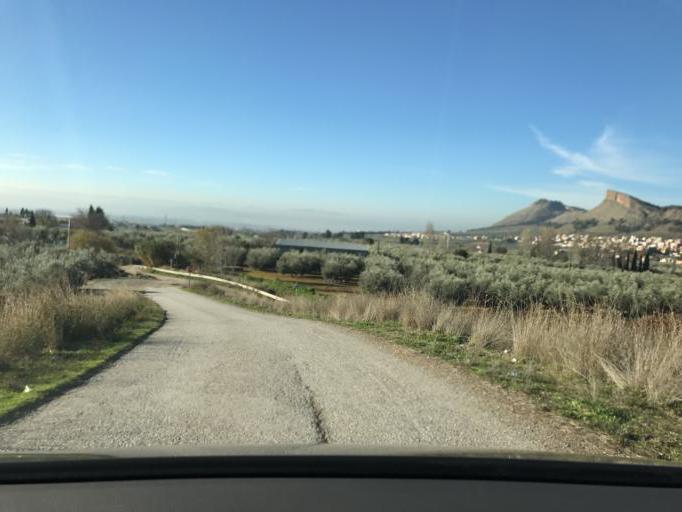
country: ES
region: Andalusia
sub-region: Provincia de Granada
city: Albolote
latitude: 37.2478
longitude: -3.6577
